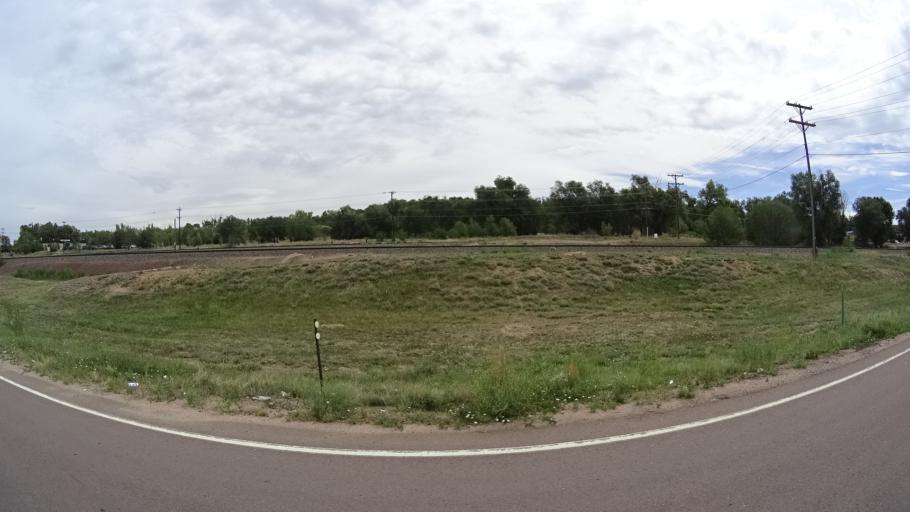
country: US
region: Colorado
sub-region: El Paso County
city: Fountain
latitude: 38.6981
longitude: -104.7064
